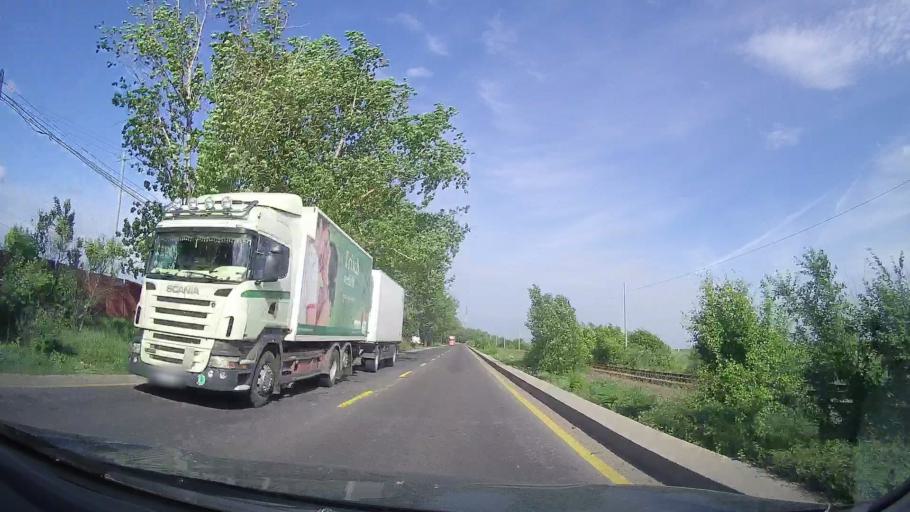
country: RO
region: Ilfov
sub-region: Comuna Magurele
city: Magurele
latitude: 44.3609
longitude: 26.0312
